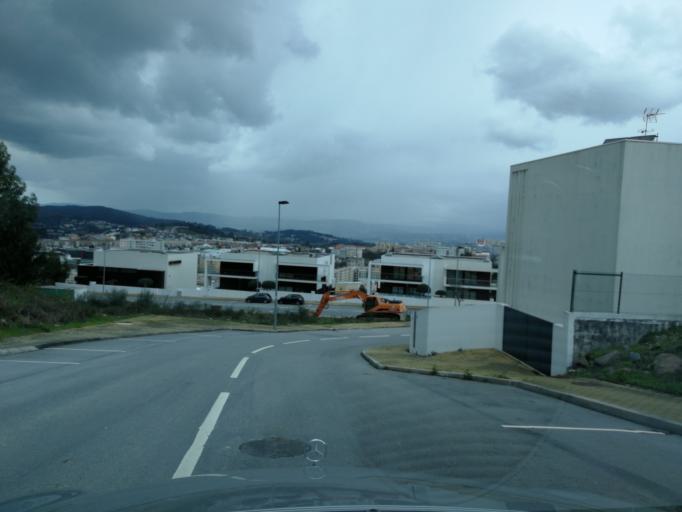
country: PT
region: Braga
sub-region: Braga
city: Braga
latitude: 41.5351
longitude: -8.4259
